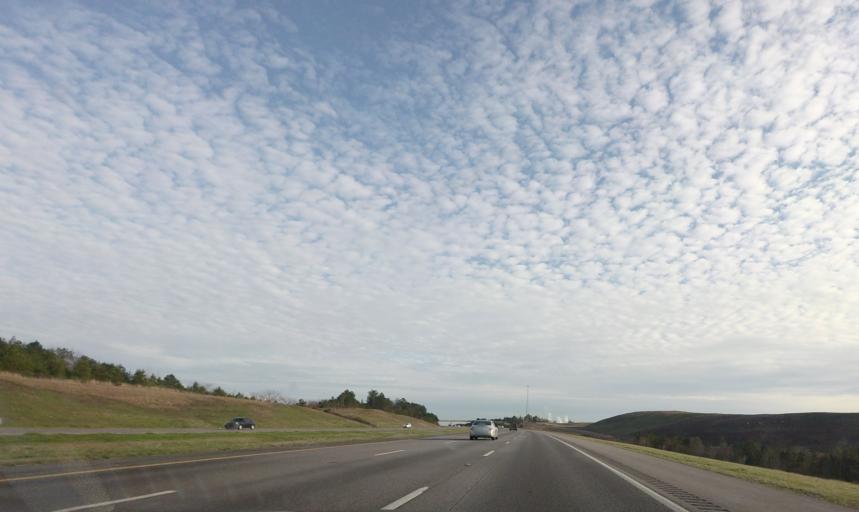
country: US
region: Alabama
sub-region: Walker County
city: Dora
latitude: 33.6978
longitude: -87.1312
